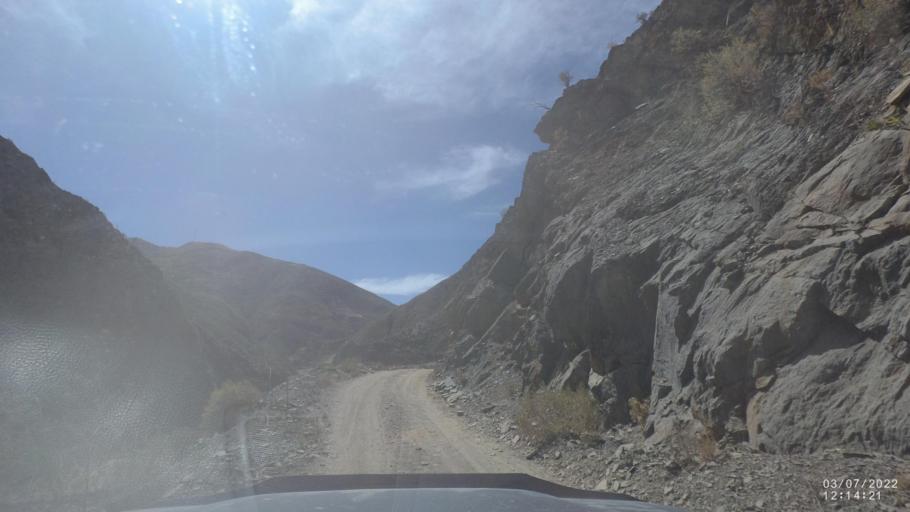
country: BO
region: Cochabamba
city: Irpa Irpa
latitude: -17.8325
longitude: -66.6096
